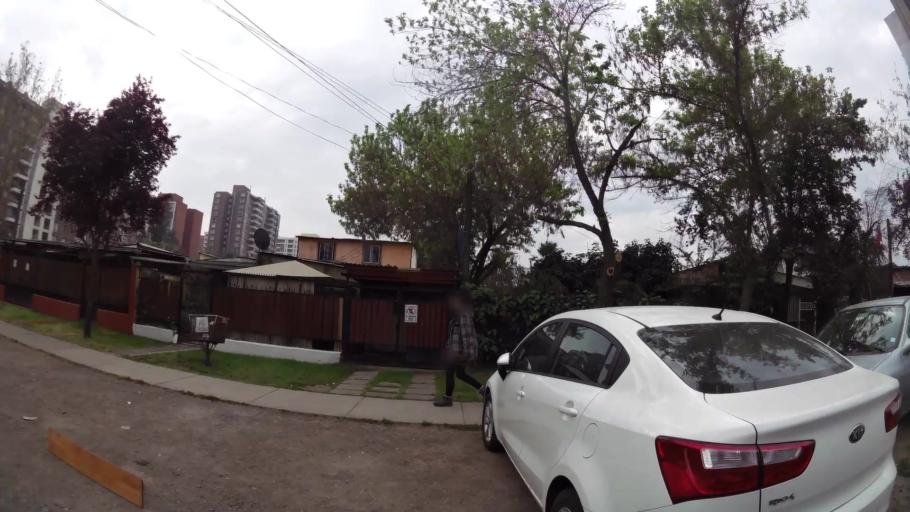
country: CL
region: Santiago Metropolitan
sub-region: Provincia de Santiago
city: Villa Presidente Frei, Nunoa, Santiago, Chile
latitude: -33.4796
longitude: -70.5965
